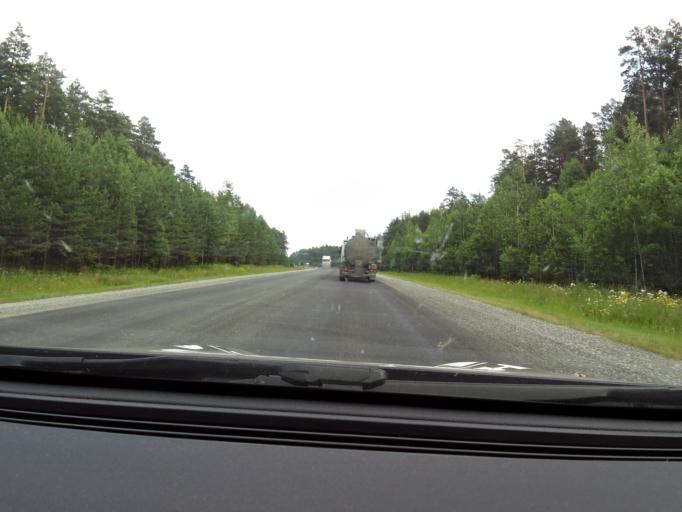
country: RU
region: Sverdlovsk
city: Achit
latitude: 56.7797
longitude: 57.9466
